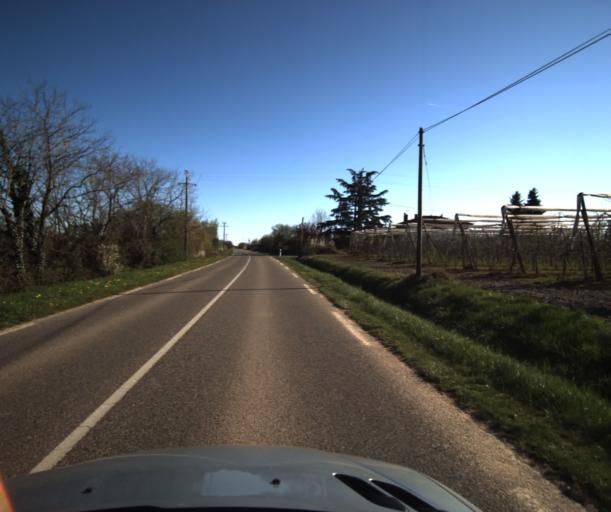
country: FR
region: Midi-Pyrenees
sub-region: Departement du Tarn-et-Garonne
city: Bressols
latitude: 43.9568
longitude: 1.3450
